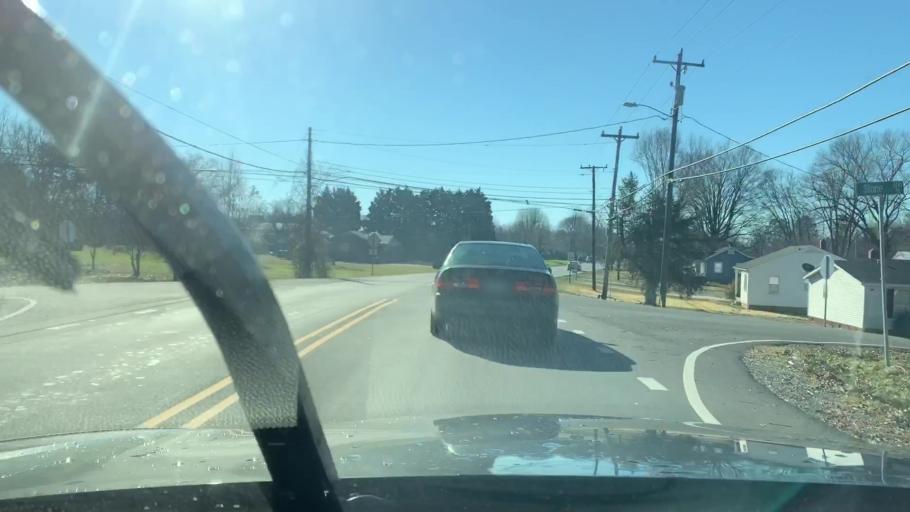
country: US
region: North Carolina
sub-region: Alamance County
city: Haw River
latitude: 36.0923
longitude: -79.3479
